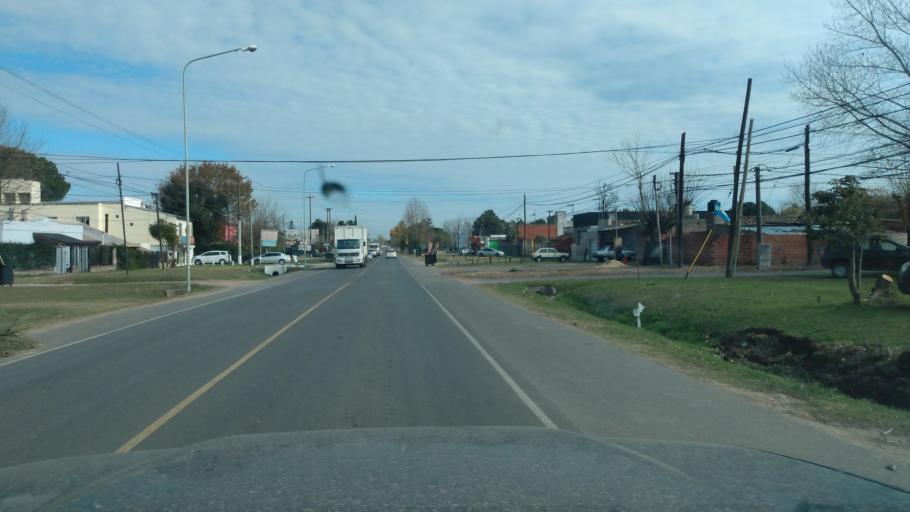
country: AR
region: Buenos Aires
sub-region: Partido de Lujan
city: Lujan
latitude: -34.5572
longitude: -59.1279
